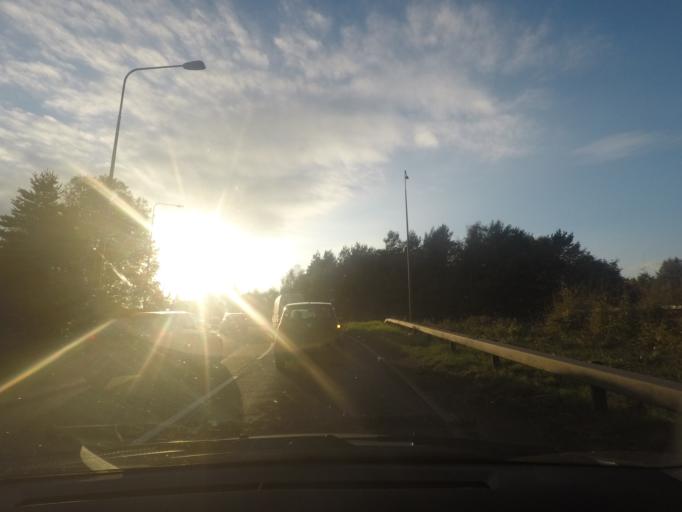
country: GB
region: England
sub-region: North Lincolnshire
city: Scawby
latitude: 53.5439
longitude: -0.5566
